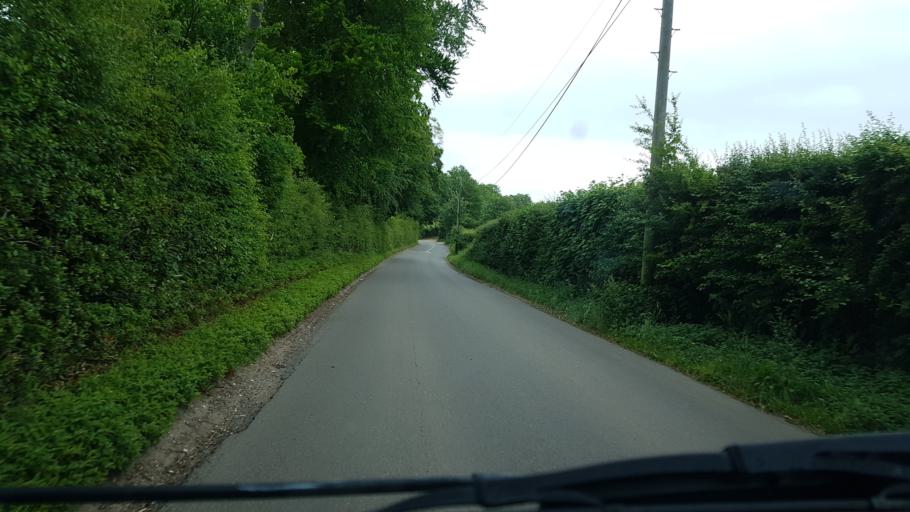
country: GB
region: England
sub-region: Surrey
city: Great Bookham
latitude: 51.2663
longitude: -0.3677
